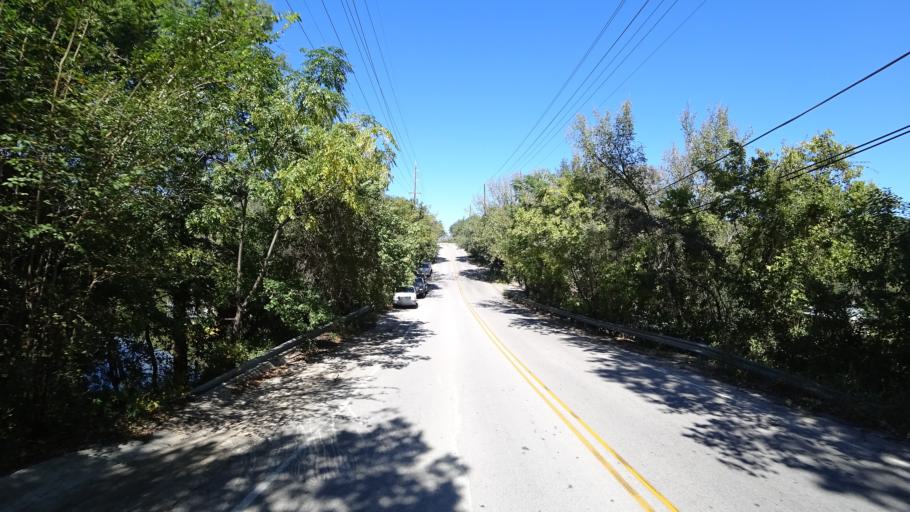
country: US
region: Texas
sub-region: Travis County
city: West Lake Hills
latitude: 30.3207
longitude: -97.7793
